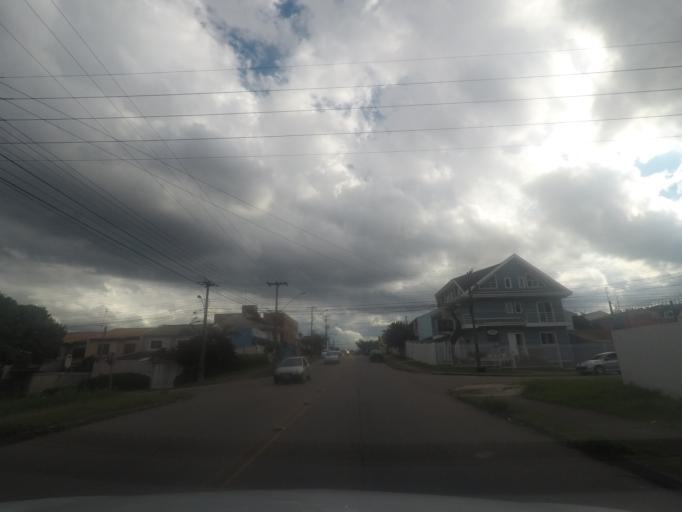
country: BR
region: Parana
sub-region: Pinhais
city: Pinhais
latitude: -25.4663
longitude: -49.2195
